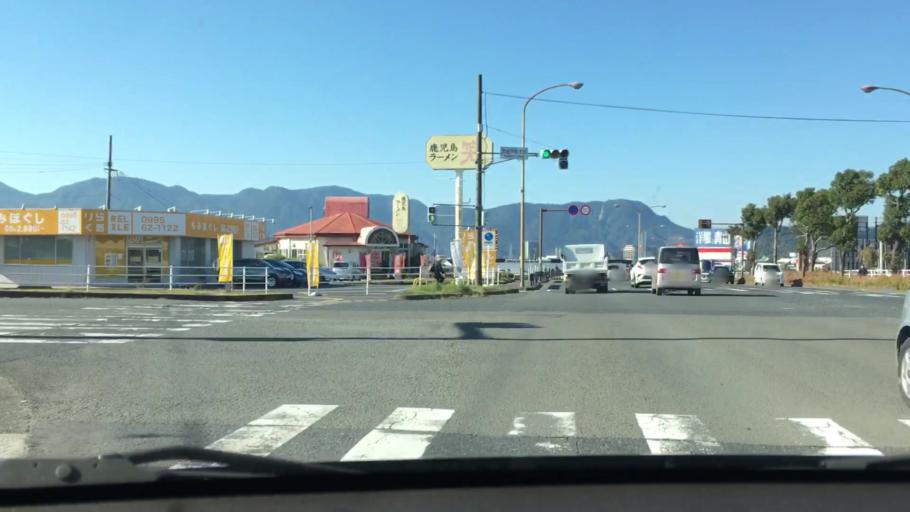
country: JP
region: Kagoshima
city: Kajiki
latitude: 31.7335
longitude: 130.6427
